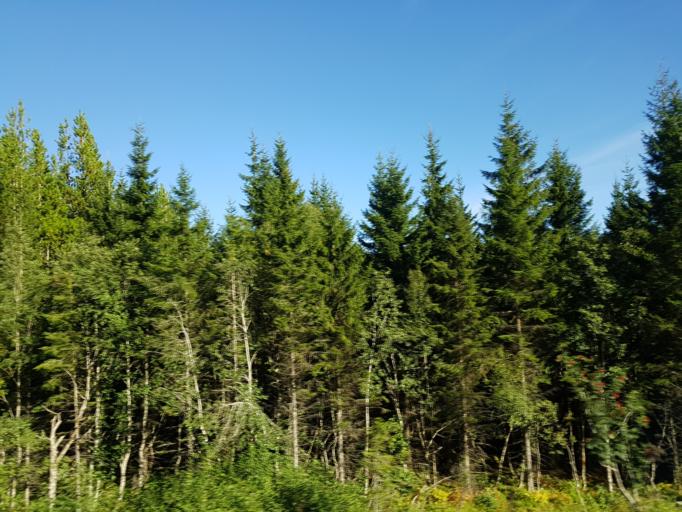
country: NO
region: Sor-Trondelag
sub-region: Afjord
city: A i Afjord
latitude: 63.6923
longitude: 10.2444
